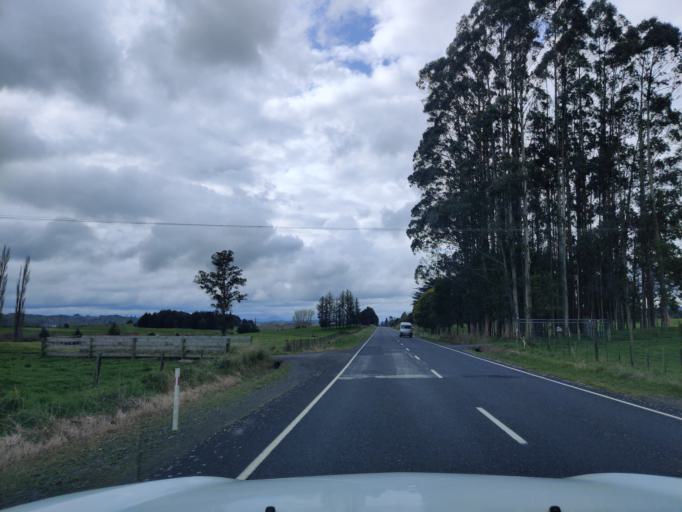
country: NZ
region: Waikato
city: Turangi
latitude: -39.0463
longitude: 175.3835
